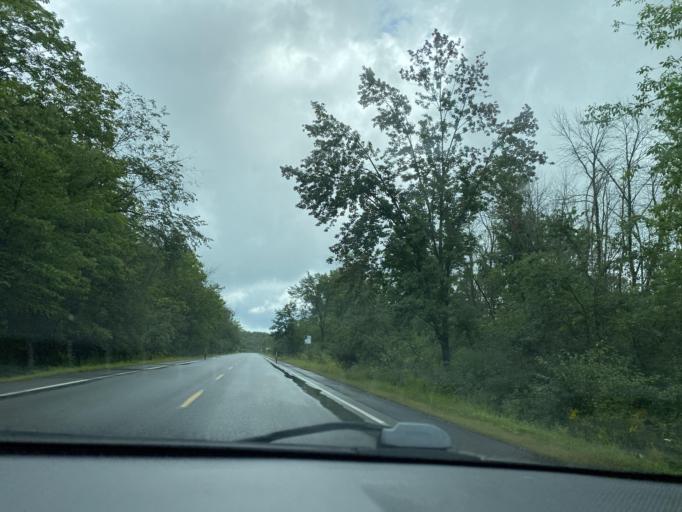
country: CA
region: Quebec
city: Baie-D'Urfe
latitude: 45.4420
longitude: -73.9118
